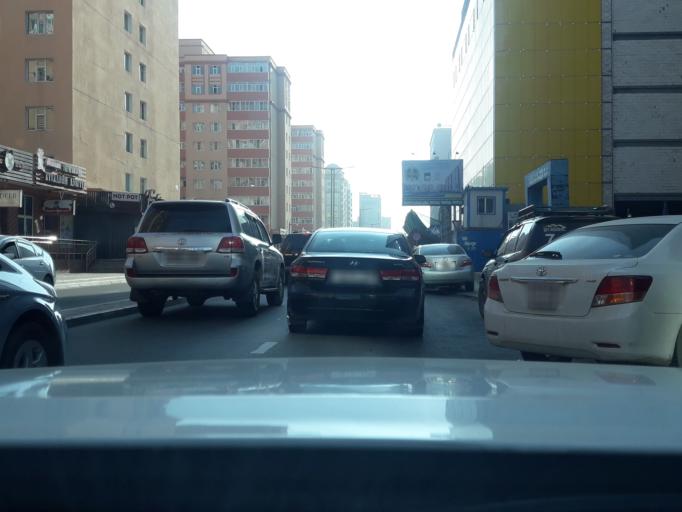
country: MN
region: Ulaanbaatar
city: Ulaanbaatar
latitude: 47.9039
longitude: 106.9350
